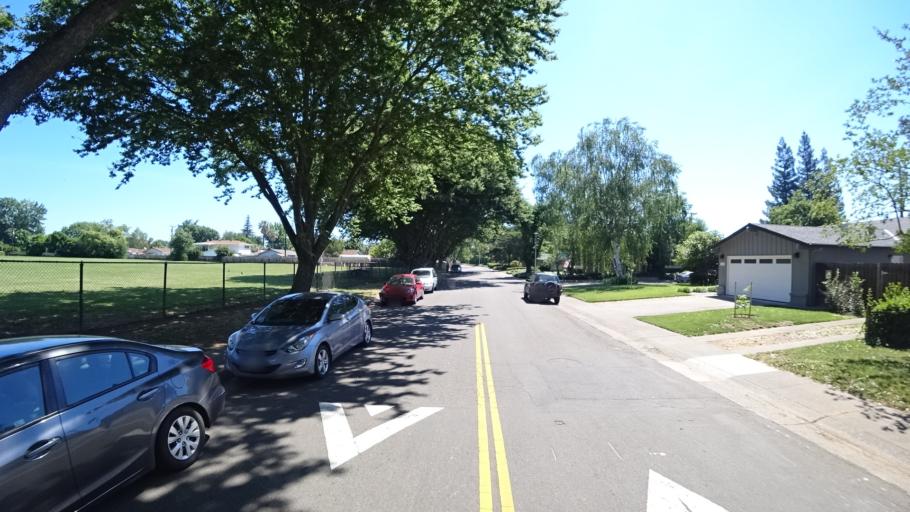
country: US
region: California
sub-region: Sacramento County
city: Rosemont
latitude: 38.5534
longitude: -121.3985
